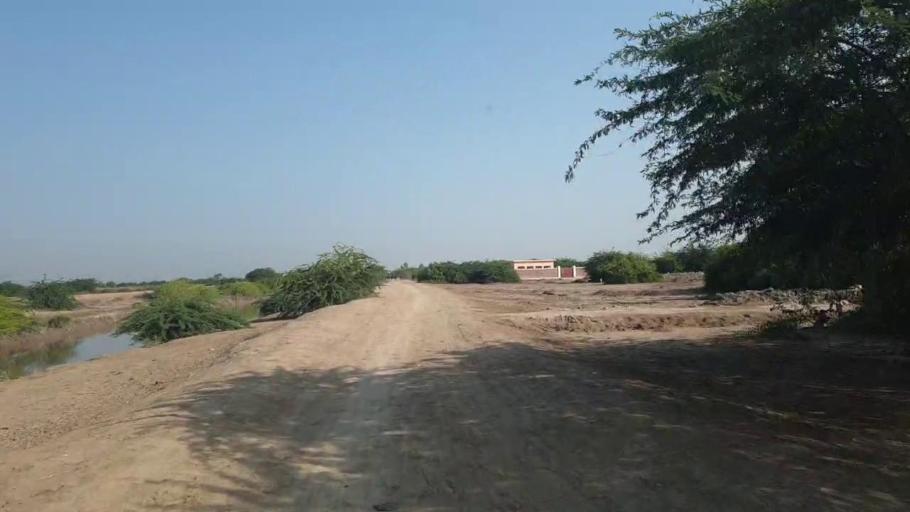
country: PK
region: Sindh
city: Badin
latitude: 24.4639
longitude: 68.7381
